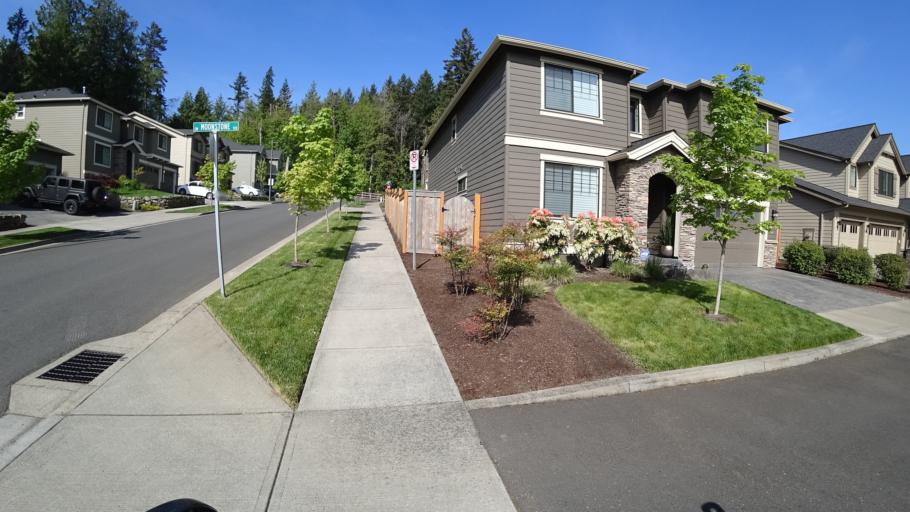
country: US
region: Oregon
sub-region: Washington County
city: Aloha
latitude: 45.4518
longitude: -122.8481
